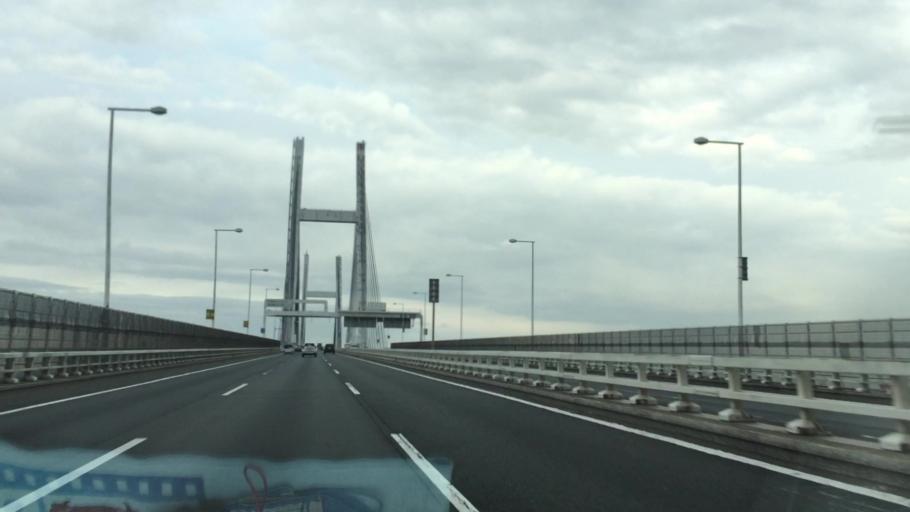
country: JP
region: Kanagawa
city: Yokohama
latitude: 35.4492
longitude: 139.6703
